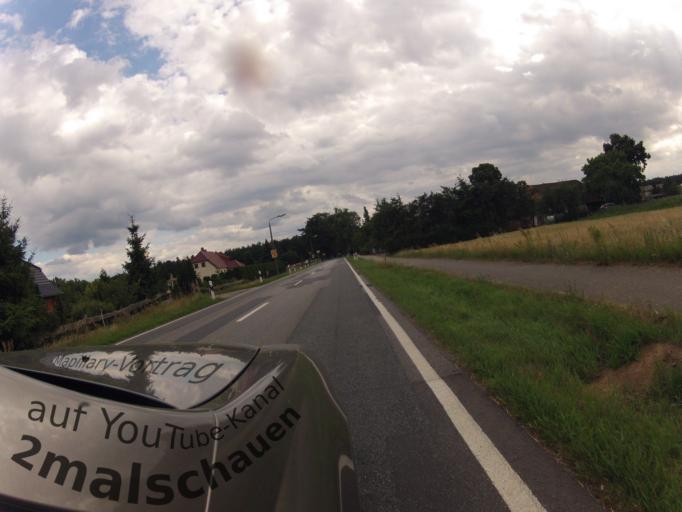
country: DE
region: Mecklenburg-Vorpommern
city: Lassan
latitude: 53.8983
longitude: 13.7864
